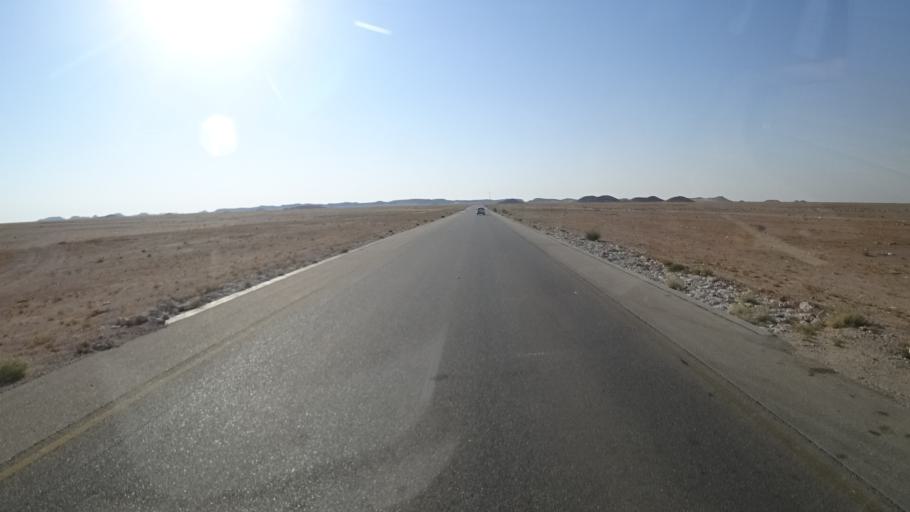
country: OM
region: Zufar
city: Salalah
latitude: 17.6390
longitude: 53.8827
